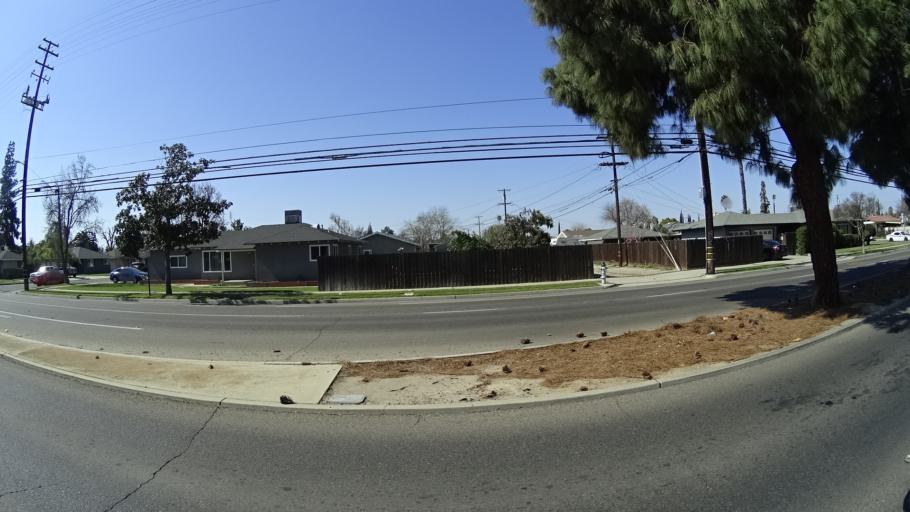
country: US
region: California
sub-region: Fresno County
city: Fresno
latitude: 36.7688
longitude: -119.8266
